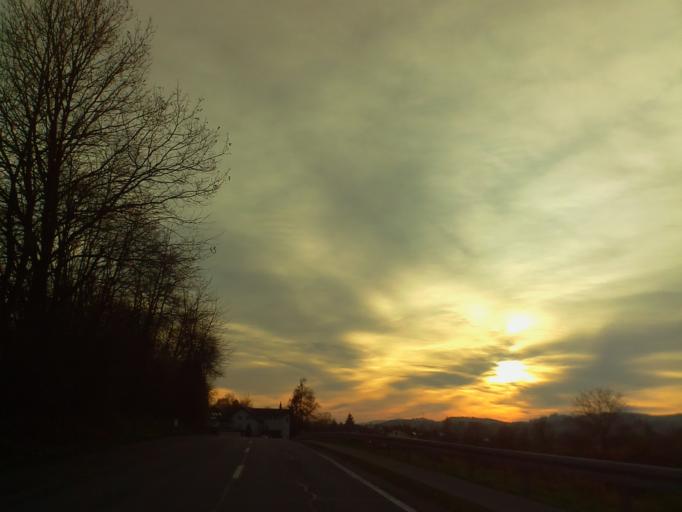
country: DE
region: Hesse
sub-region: Regierungsbezirk Darmstadt
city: Furth
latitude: 49.6428
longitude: 8.7732
